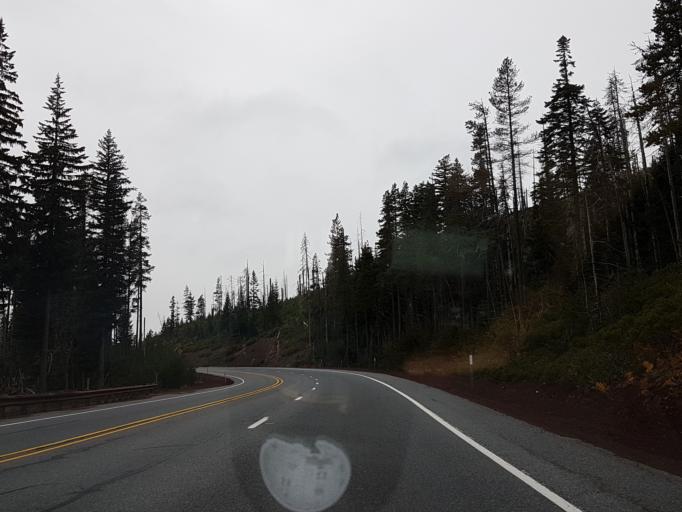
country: US
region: Oregon
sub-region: Deschutes County
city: Sisters
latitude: 44.4235
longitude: -121.8282
